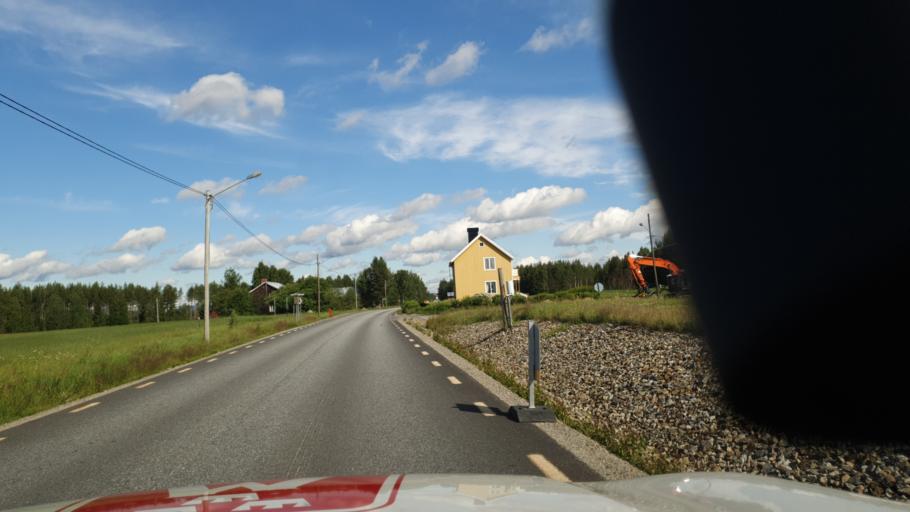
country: SE
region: Vaesterbotten
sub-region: Norsjo Kommun
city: Norsjoe
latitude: 64.5405
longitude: 19.3368
